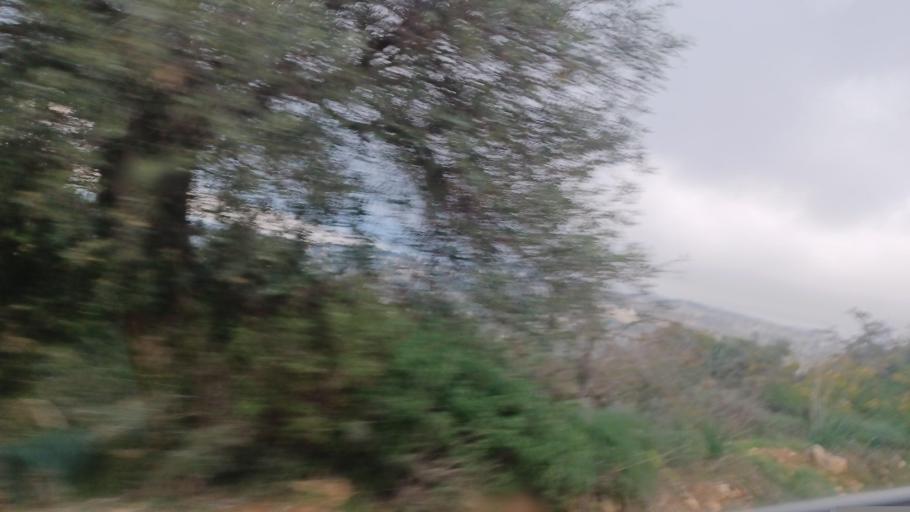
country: CY
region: Pafos
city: Mesogi
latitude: 34.7857
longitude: 32.4976
